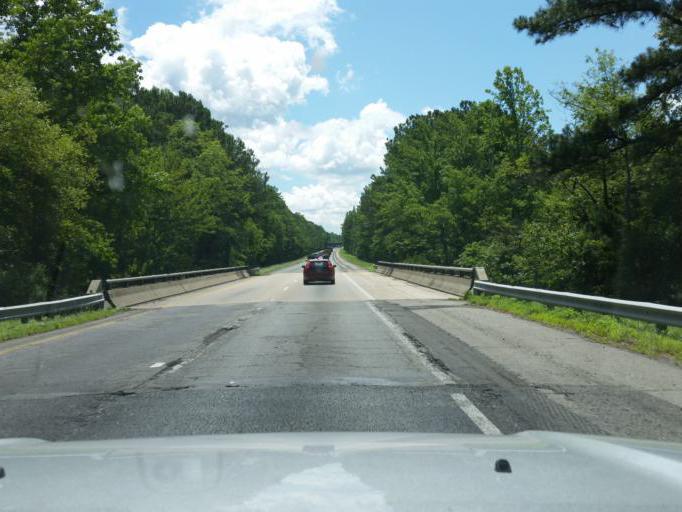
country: US
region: Virginia
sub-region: King William County
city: West Point
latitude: 37.4533
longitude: -76.8726
